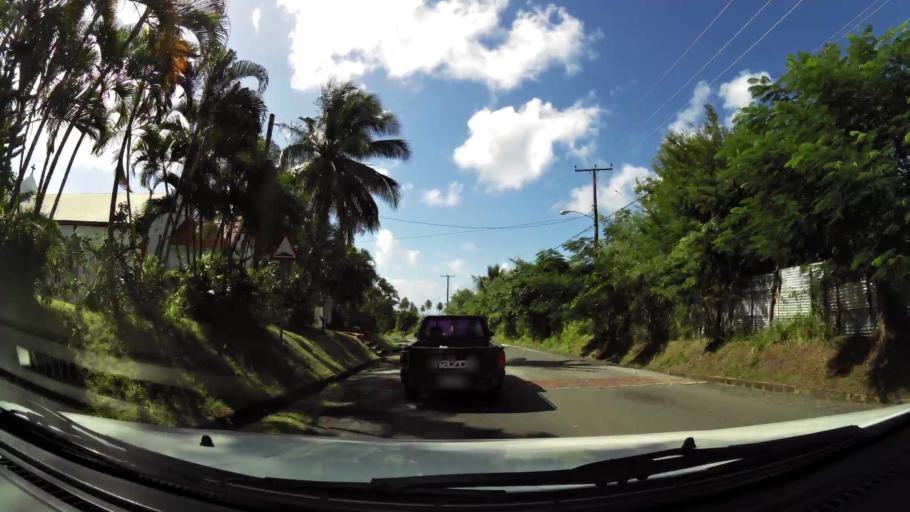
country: LC
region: Choiseul Quarter
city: Choiseul
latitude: 13.7650
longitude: -61.0363
